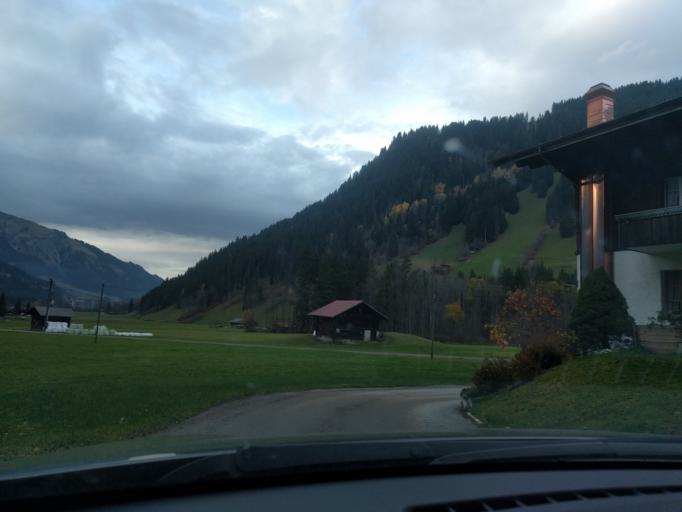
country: CH
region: Bern
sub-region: Obersimmental-Saanen District
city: Lenk
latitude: 46.4266
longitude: 7.4760
